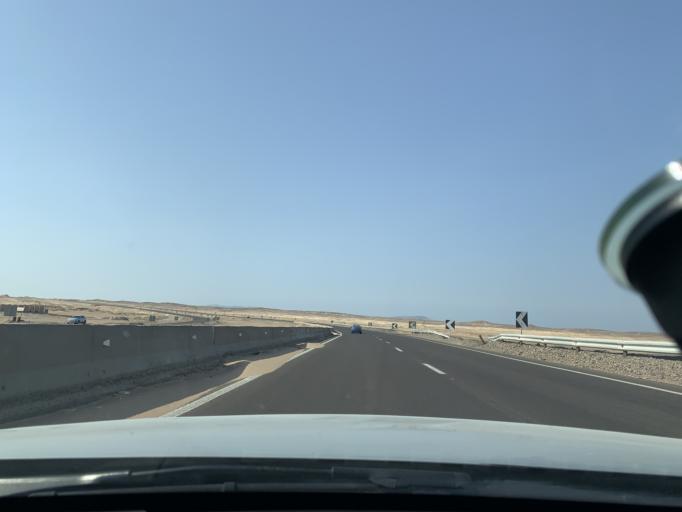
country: EG
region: Red Sea
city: El Gouna
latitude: 27.7323
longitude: 33.5083
